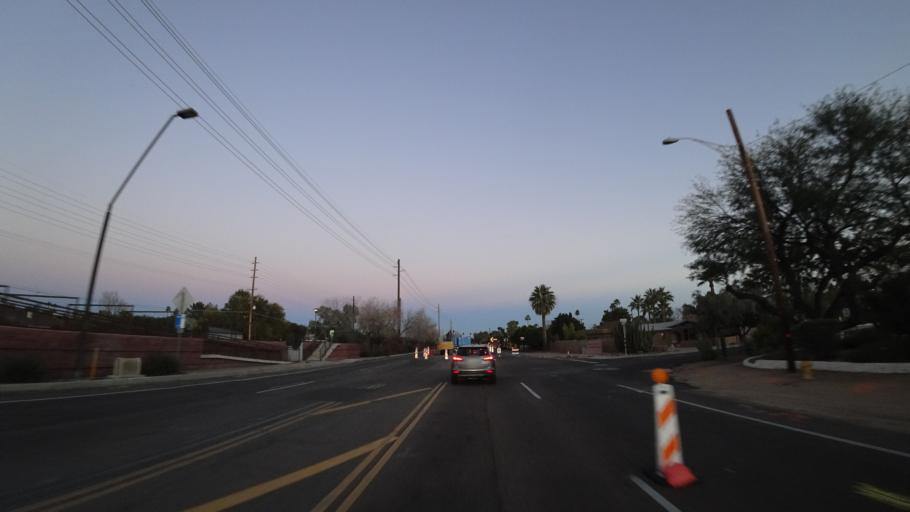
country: US
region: Arizona
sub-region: Maricopa County
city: Paradise Valley
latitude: 33.4906
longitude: -111.9524
